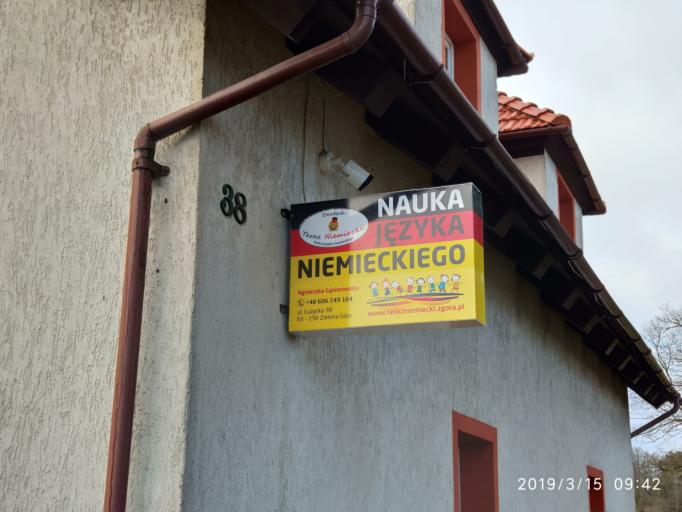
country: PL
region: Lubusz
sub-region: Zielona Gora
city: Zielona Gora
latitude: 51.9299
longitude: 15.4758
